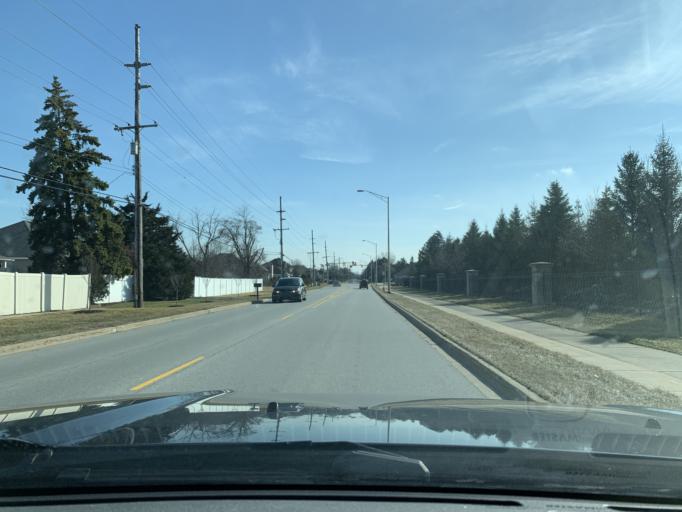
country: US
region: Indiana
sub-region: Lake County
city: Munster
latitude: 41.5325
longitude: -87.4904
